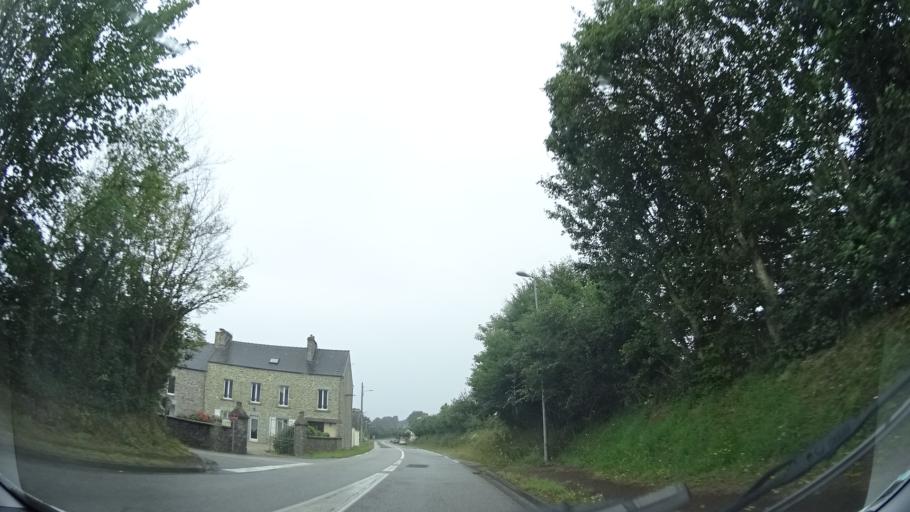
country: FR
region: Lower Normandy
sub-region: Departement de la Manche
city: Martinvast
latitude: 49.6200
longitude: -1.6670
